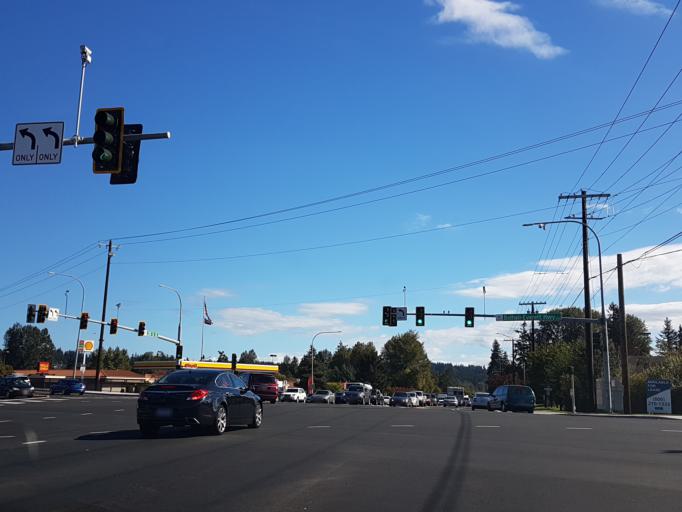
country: US
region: Washington
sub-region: King County
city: Bothell
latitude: 47.7913
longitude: -122.2170
